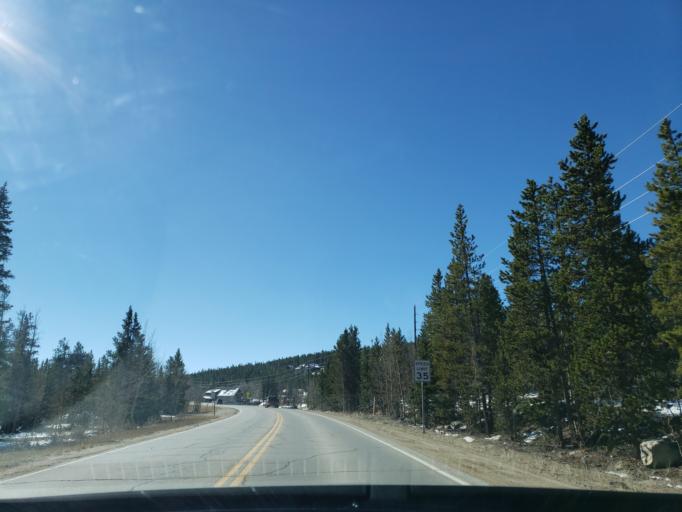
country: US
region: Colorado
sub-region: Park County
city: Fairplay
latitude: 39.2917
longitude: -106.0665
